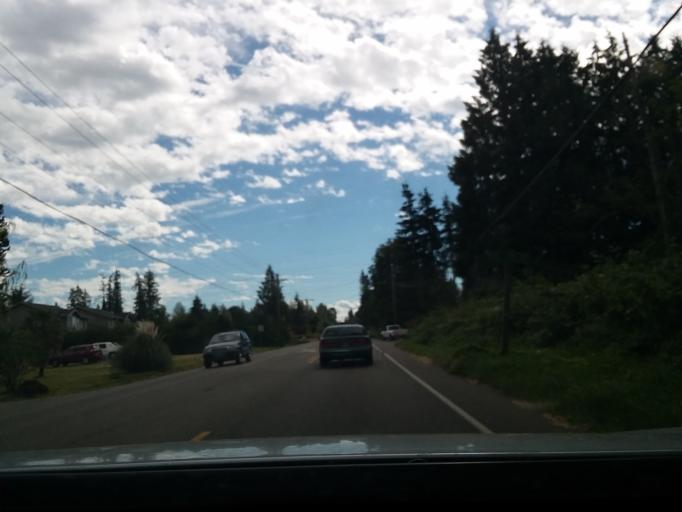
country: US
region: Washington
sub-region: Snohomish County
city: West Lake Stevens
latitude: 47.9781
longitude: -122.1162
